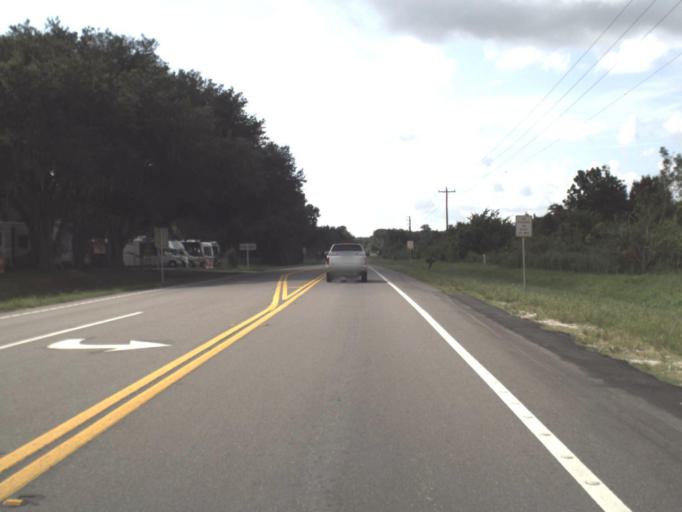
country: US
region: Florida
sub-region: Pasco County
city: Zephyrhills South
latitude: 28.2065
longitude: -82.1744
